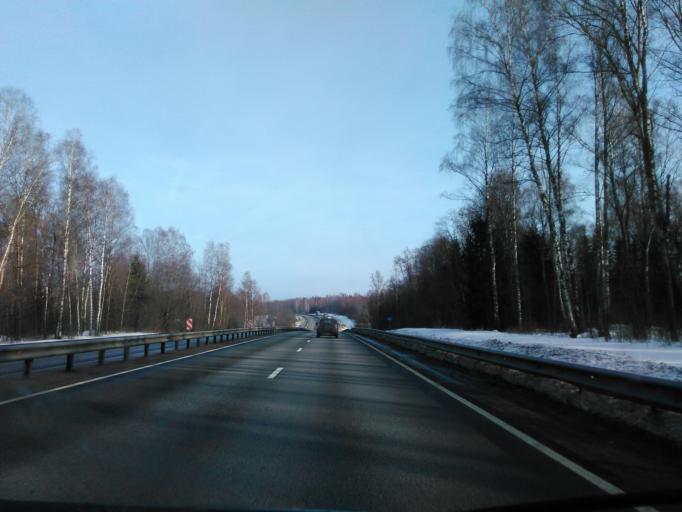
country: RU
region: Smolensk
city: Vyaz'ma
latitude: 55.1925
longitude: 33.9473
